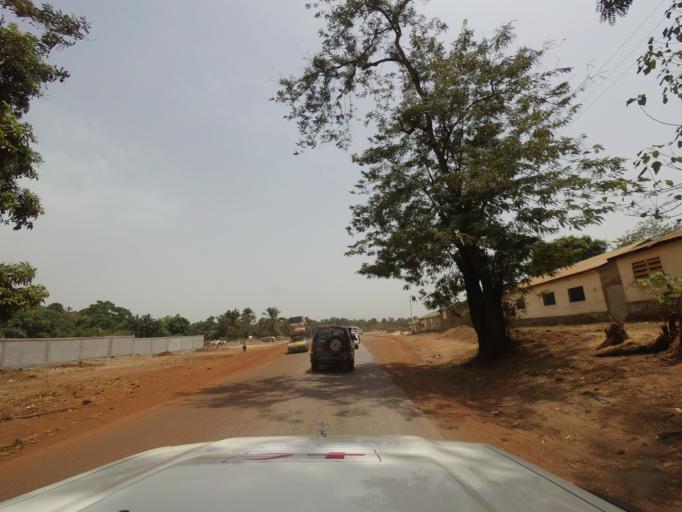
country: GN
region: Kindia
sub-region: Coyah
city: Coyah
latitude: 9.7194
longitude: -13.3729
